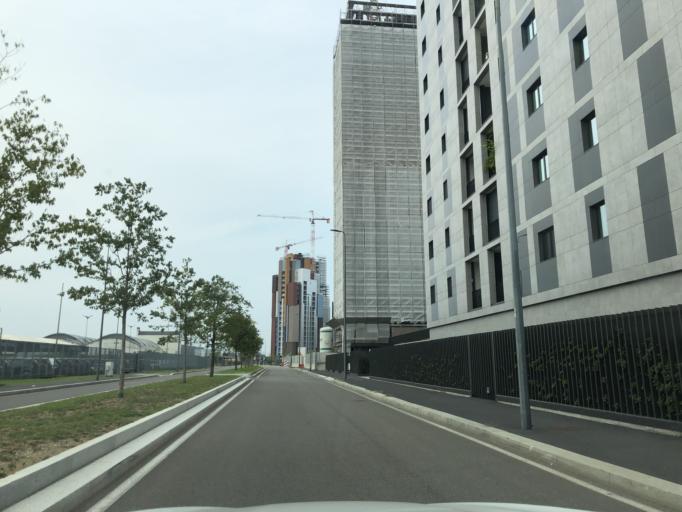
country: IT
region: Lombardy
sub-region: Citta metropolitana di Milano
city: Pero
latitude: 45.5081
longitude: 9.1003
